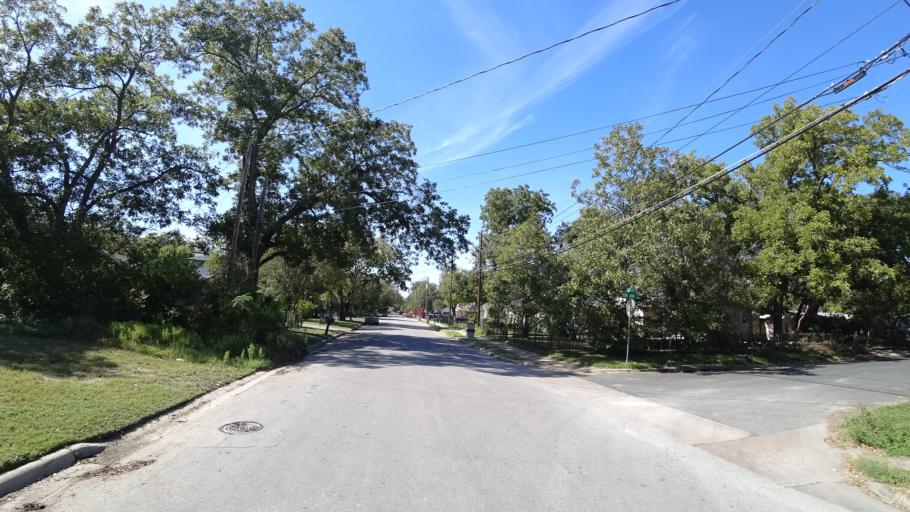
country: US
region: Texas
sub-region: Travis County
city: Austin
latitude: 30.2674
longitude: -97.6906
